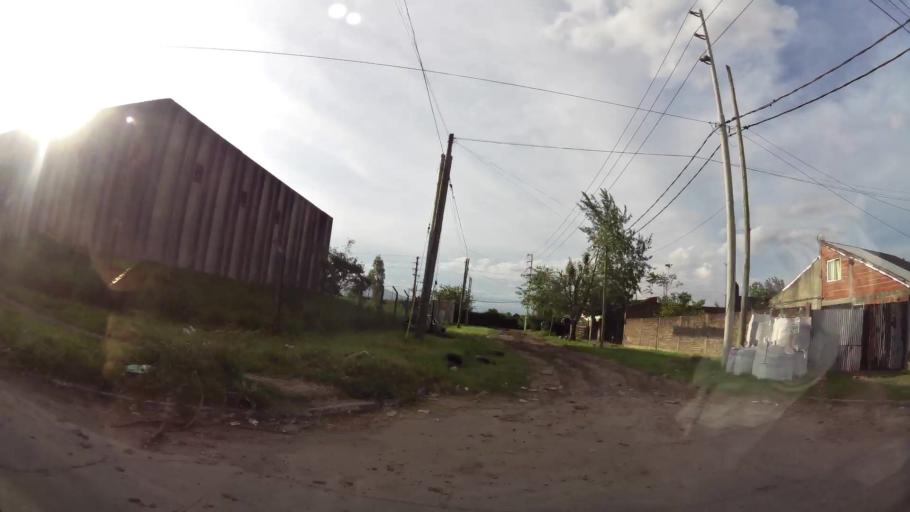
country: AR
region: Buenos Aires
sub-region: Partido de Quilmes
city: Quilmes
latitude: -34.7515
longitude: -58.2601
